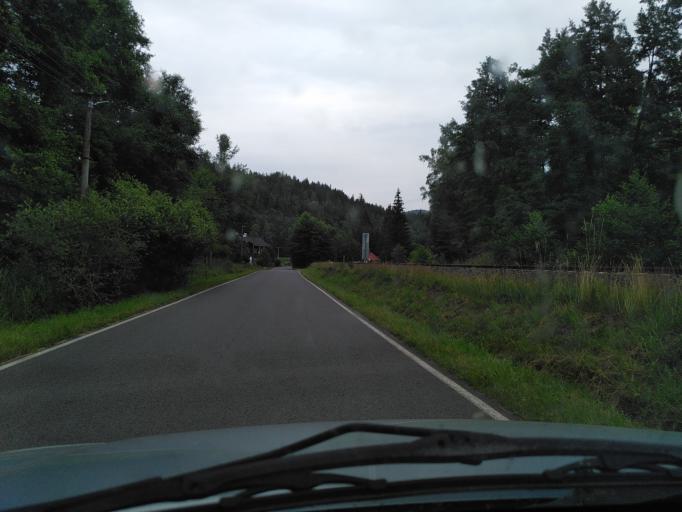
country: CZ
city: Kamenicky Senov
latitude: 50.8124
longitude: 14.5064
